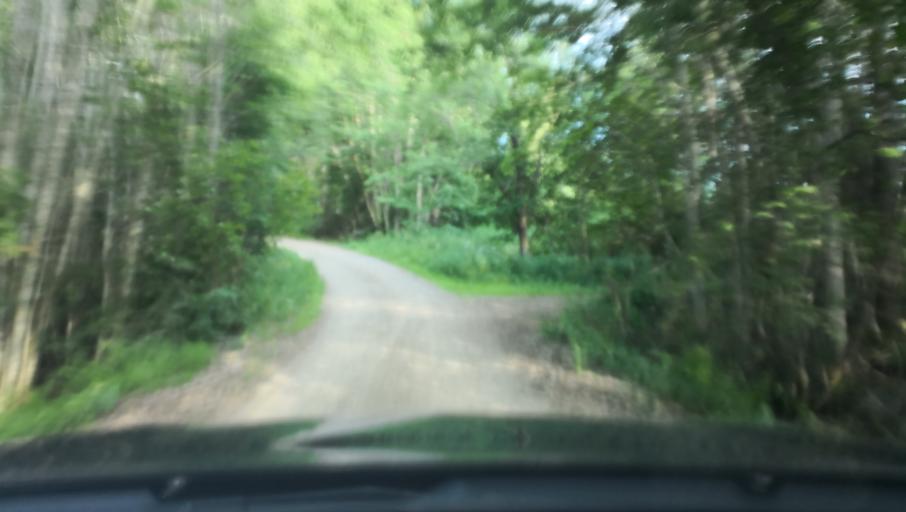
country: SE
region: Dalarna
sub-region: Ludvika Kommun
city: Ludvika
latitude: 60.0750
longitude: 15.2669
